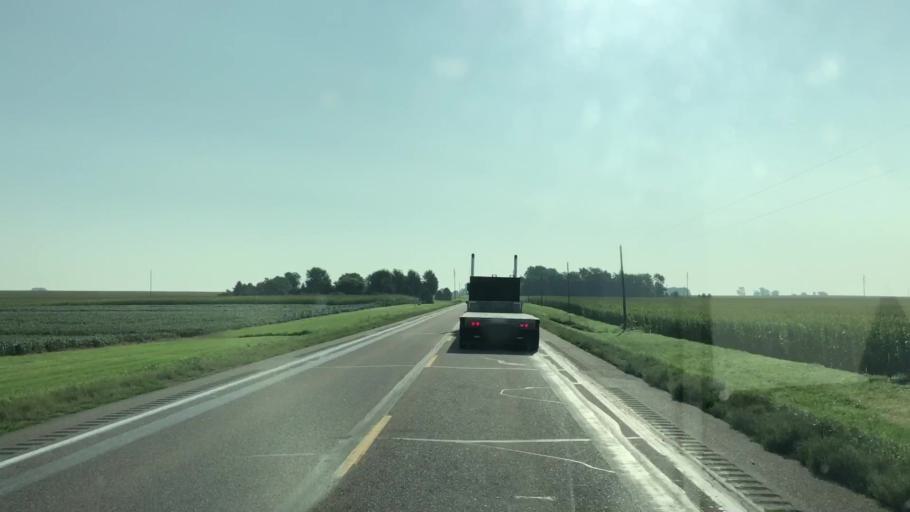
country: US
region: Iowa
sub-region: O'Brien County
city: Sheldon
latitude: 43.1862
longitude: -95.9861
